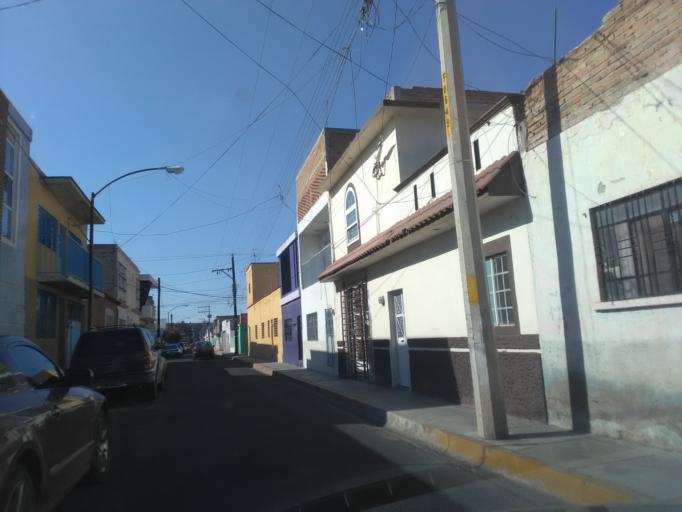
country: MX
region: Durango
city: Victoria de Durango
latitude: 24.0317
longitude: -104.6631
